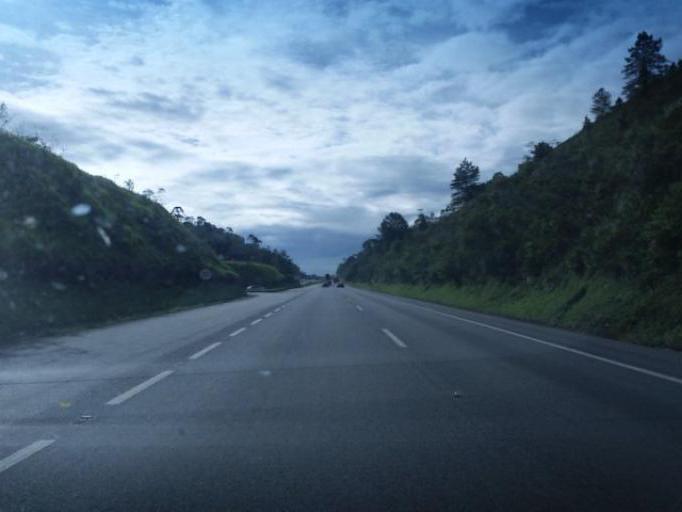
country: BR
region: Parana
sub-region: Antonina
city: Antonina
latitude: -25.1039
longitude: -48.7173
